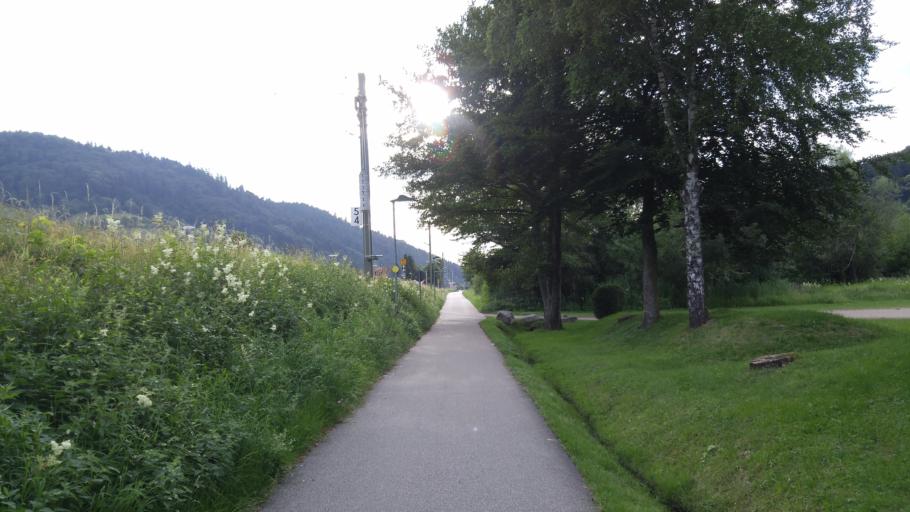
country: DE
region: Baden-Wuerttemberg
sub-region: Freiburg Region
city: Muenstertal/Schwarzwald
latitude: 47.8561
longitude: 7.7771
